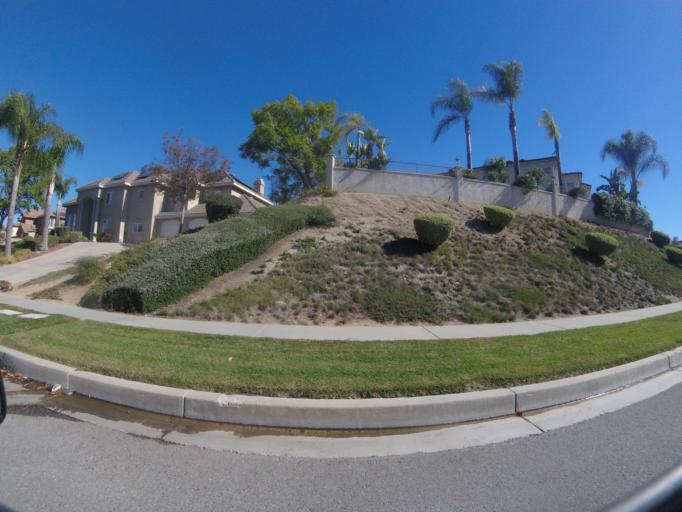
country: US
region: California
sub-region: San Bernardino County
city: Mentone
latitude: 34.0266
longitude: -117.1381
